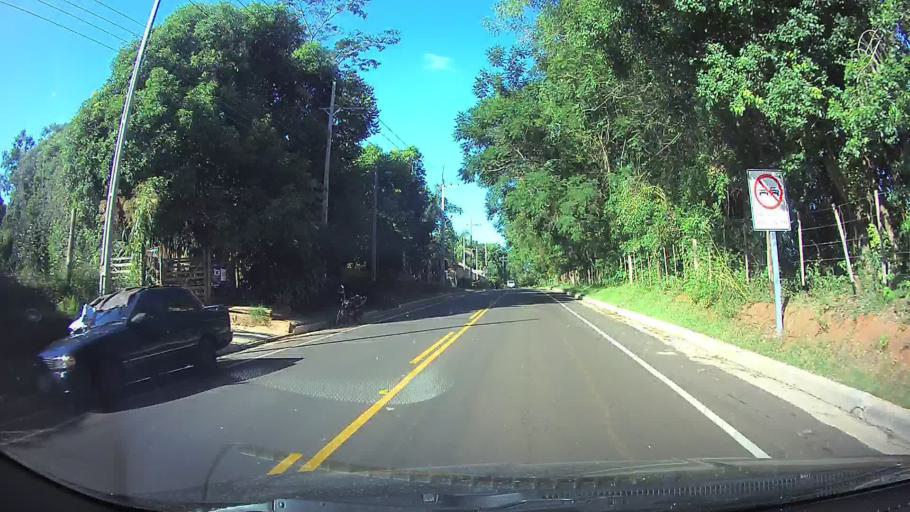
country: PY
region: Cordillera
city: Caacupe
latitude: -25.3200
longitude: -57.1473
